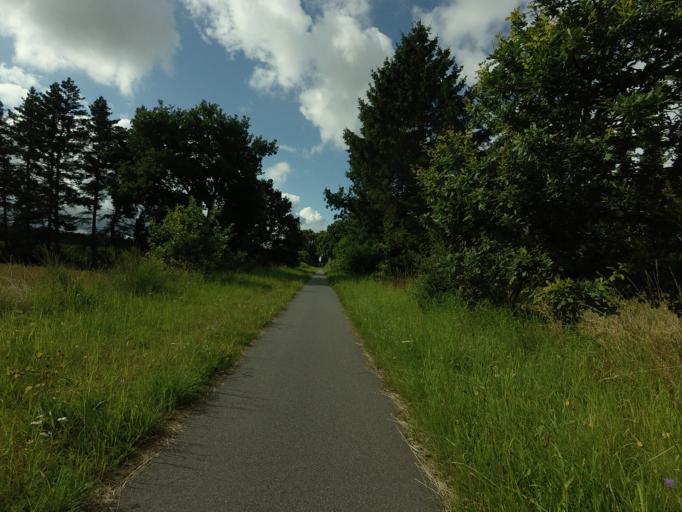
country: DK
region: Central Jutland
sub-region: Silkeborg Kommune
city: Svejbaek
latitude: 56.2028
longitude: 9.6689
